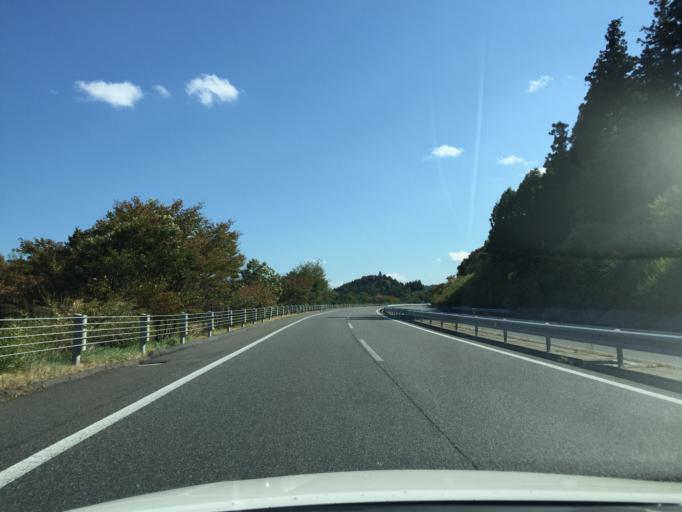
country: JP
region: Fukushima
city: Funehikimachi-funehiki
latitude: 37.2528
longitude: 140.6568
